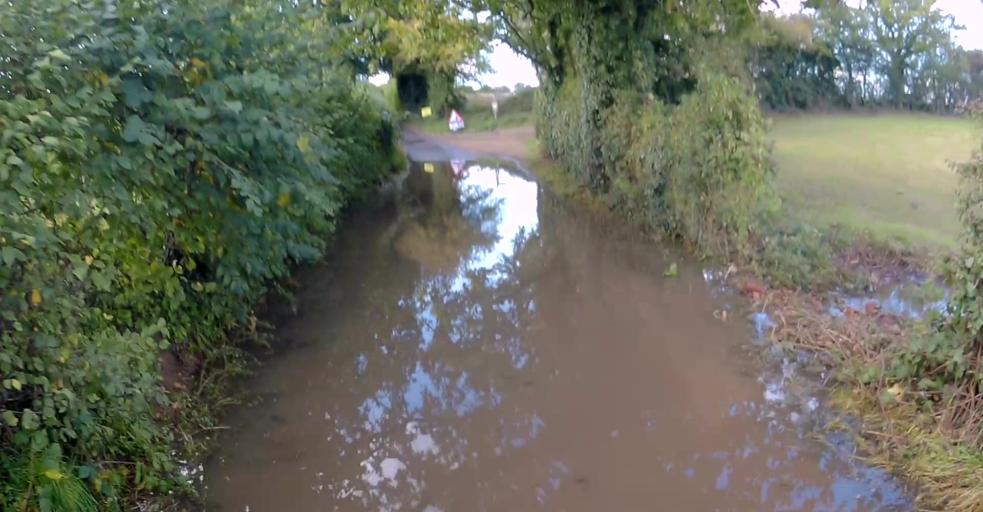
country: GB
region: England
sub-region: Surrey
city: Farnham
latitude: 51.2074
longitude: -0.8476
